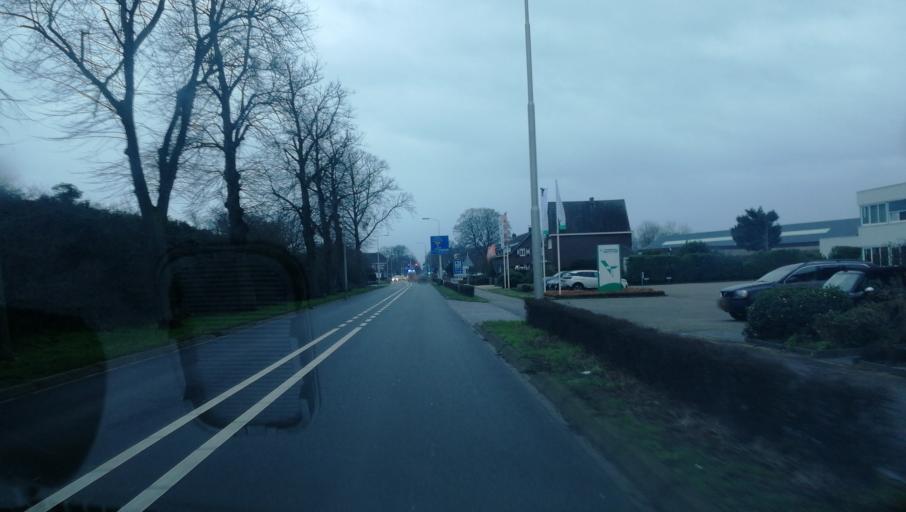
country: NL
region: Limburg
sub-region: Gemeente Venlo
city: Tegelen
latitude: 51.3337
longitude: 6.0940
